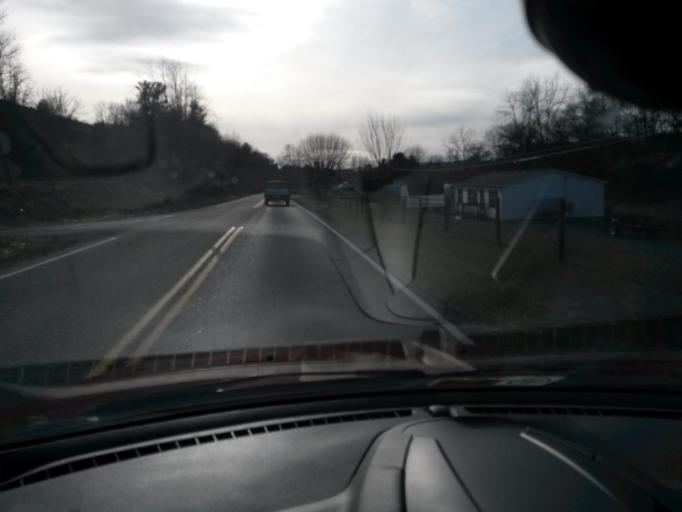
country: US
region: Virginia
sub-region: Rockbridge County
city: East Lexington
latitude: 38.0540
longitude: -79.4168
